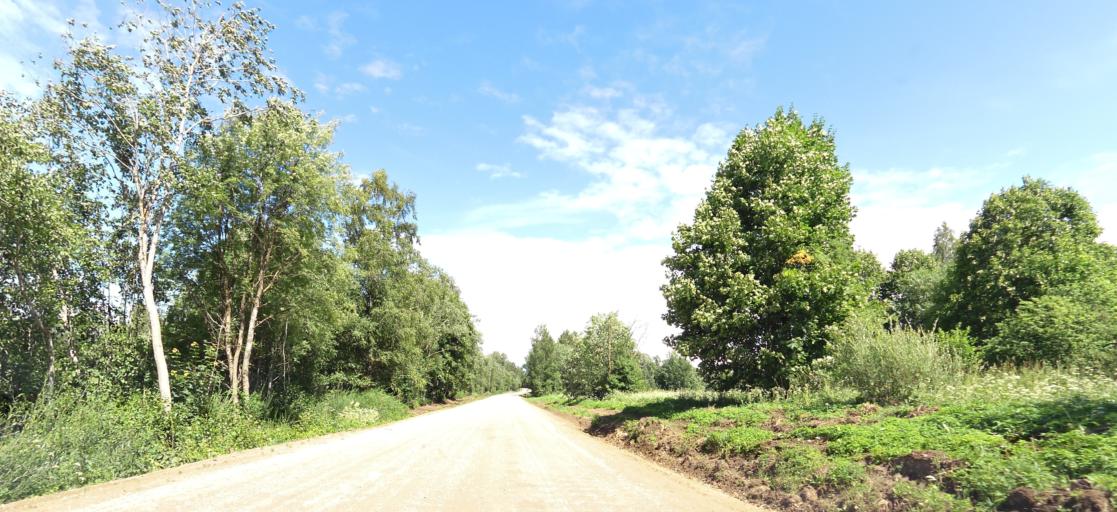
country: LT
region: Panevezys
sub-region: Birzai
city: Birzai
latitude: 56.4065
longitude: 24.7925
